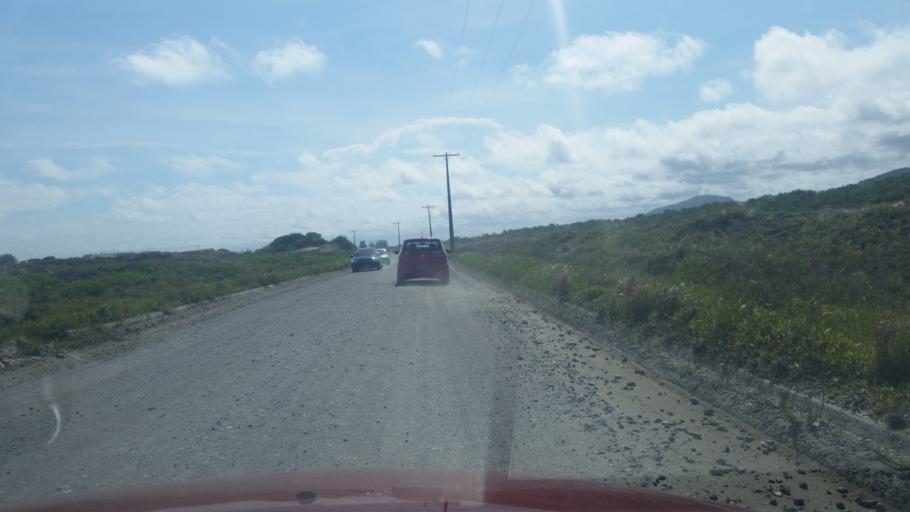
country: BR
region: Sao Paulo
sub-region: Iguape
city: Iguape
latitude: -24.7022
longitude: -47.4666
